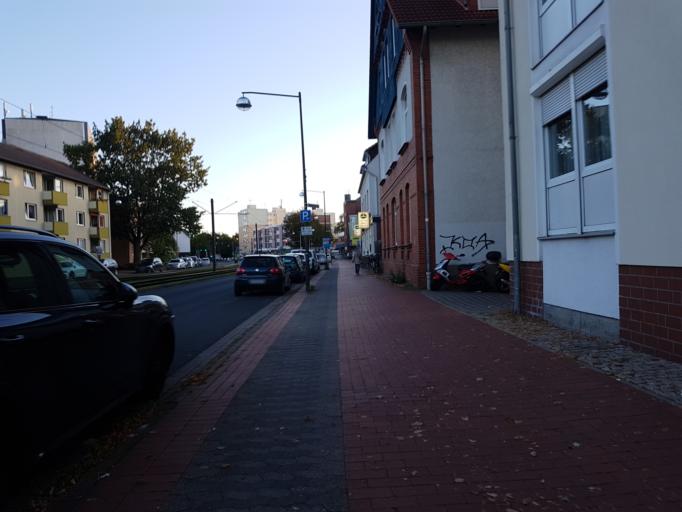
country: DE
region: Lower Saxony
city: Langenhagen
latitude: 52.4349
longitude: 9.7319
